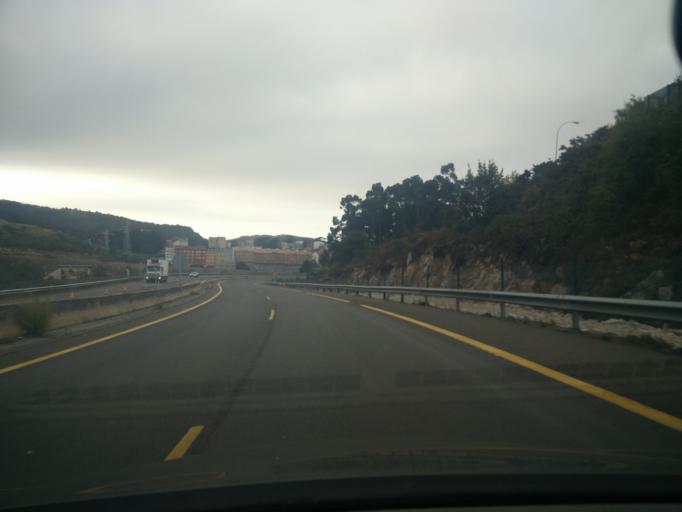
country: ES
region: Galicia
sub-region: Provincia da Coruna
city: Arteixo
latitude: 43.3349
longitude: -8.4546
